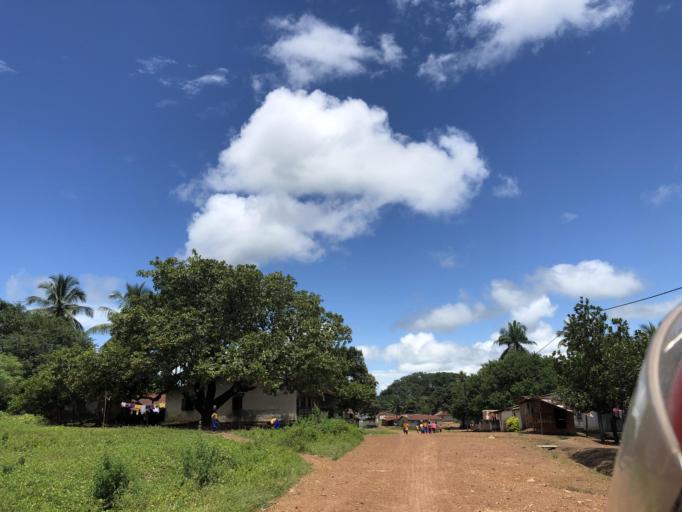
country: SL
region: Northern Province
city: Makeni
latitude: 8.8661
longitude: -12.1256
